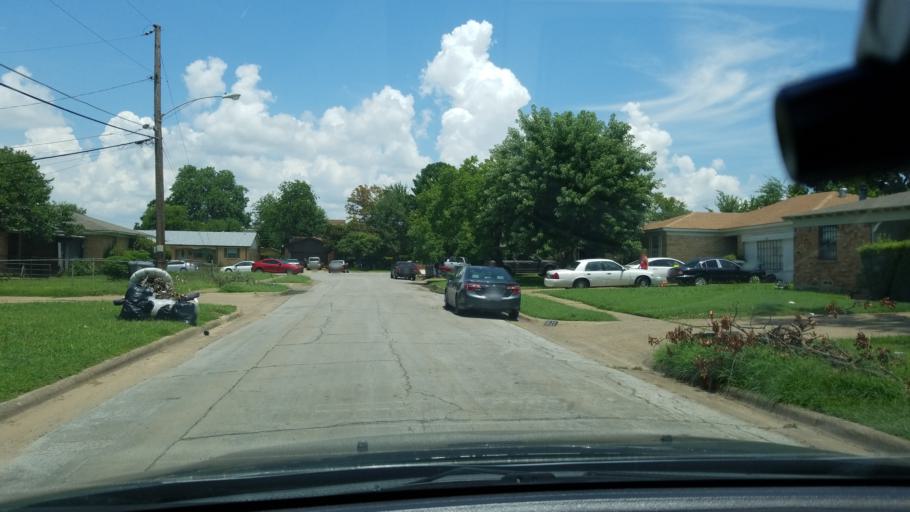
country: US
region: Texas
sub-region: Dallas County
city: Balch Springs
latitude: 32.7384
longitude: -96.6490
